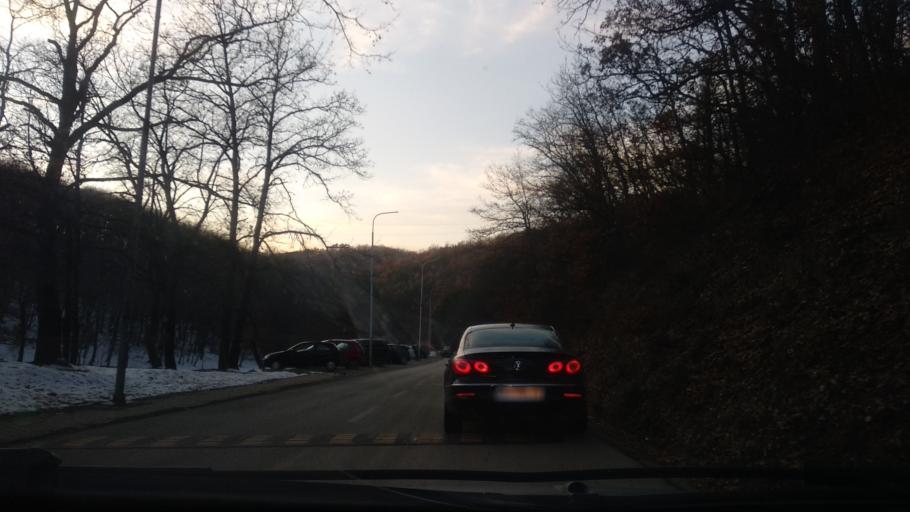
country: XK
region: Pristina
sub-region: Komuna e Prishtines
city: Pristina
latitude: 42.6755
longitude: 21.2118
